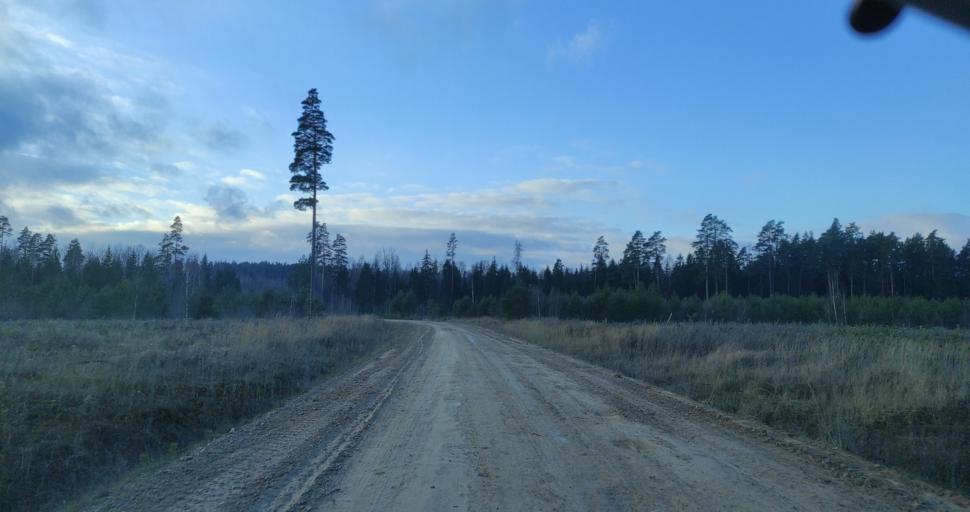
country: LV
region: Kuldigas Rajons
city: Kuldiga
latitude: 57.0551
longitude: 21.8502
